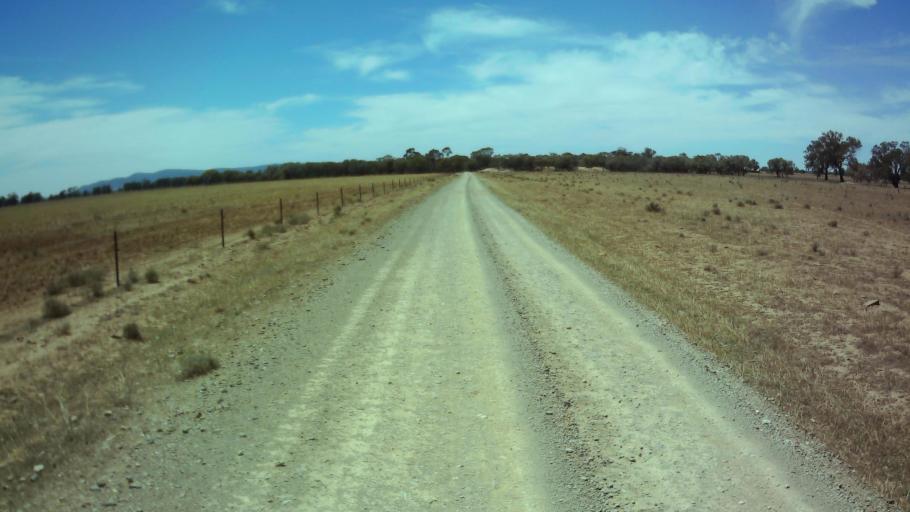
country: AU
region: New South Wales
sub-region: Weddin
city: Grenfell
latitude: -33.8662
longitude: 147.7642
